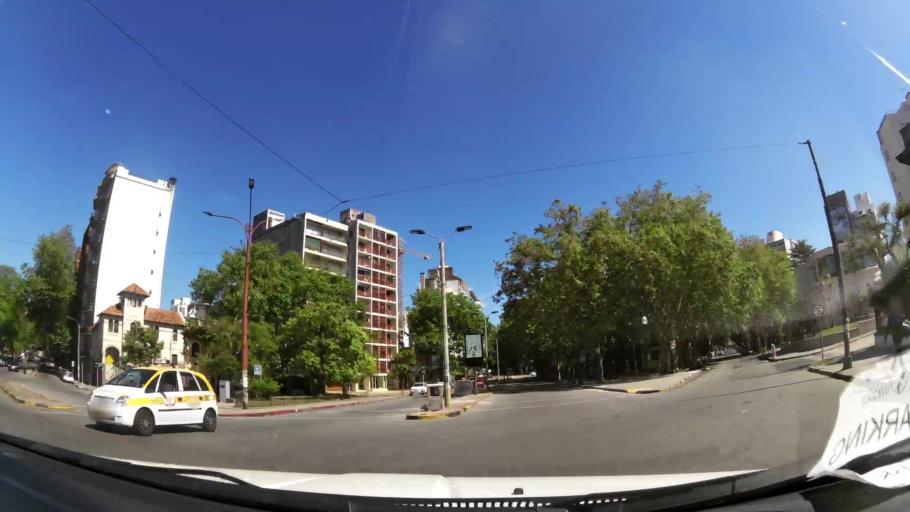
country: UY
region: Montevideo
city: Montevideo
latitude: -34.9113
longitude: -56.1656
